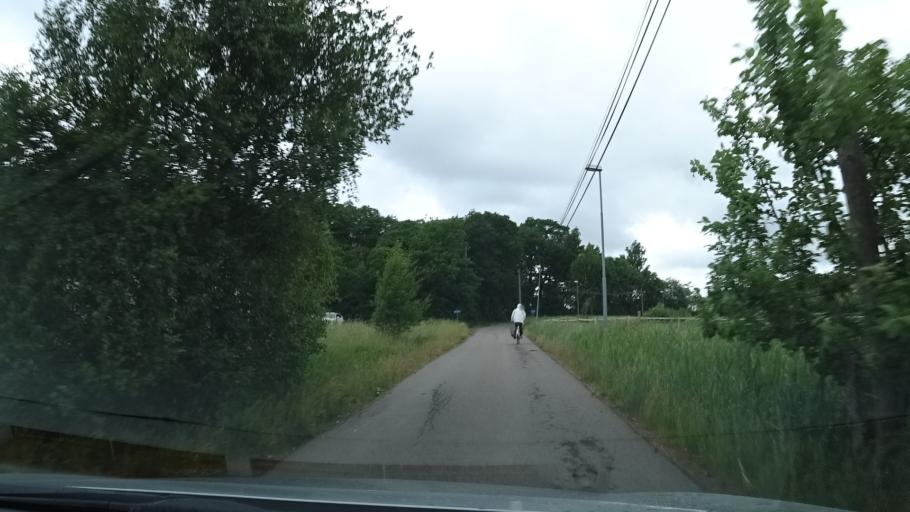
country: SE
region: Vaestra Goetaland
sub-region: Goteborg
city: Billdal
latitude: 57.5830
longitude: 11.9539
